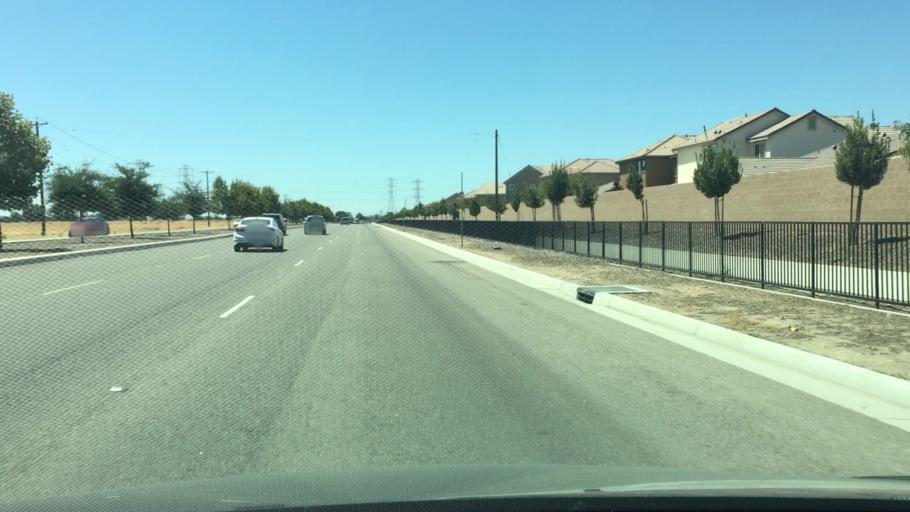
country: US
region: California
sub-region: Fresno County
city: Biola
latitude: 36.8369
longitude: -119.8943
